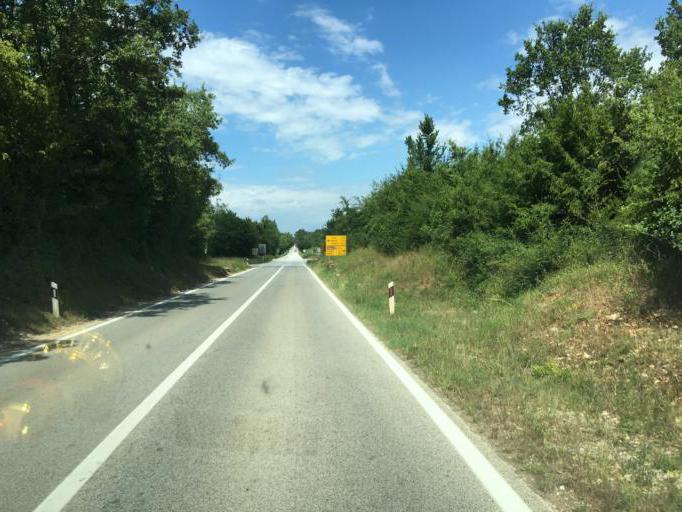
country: HR
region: Istarska
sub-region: Grad Rovinj
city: Rovinj
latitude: 45.1637
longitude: 13.7424
